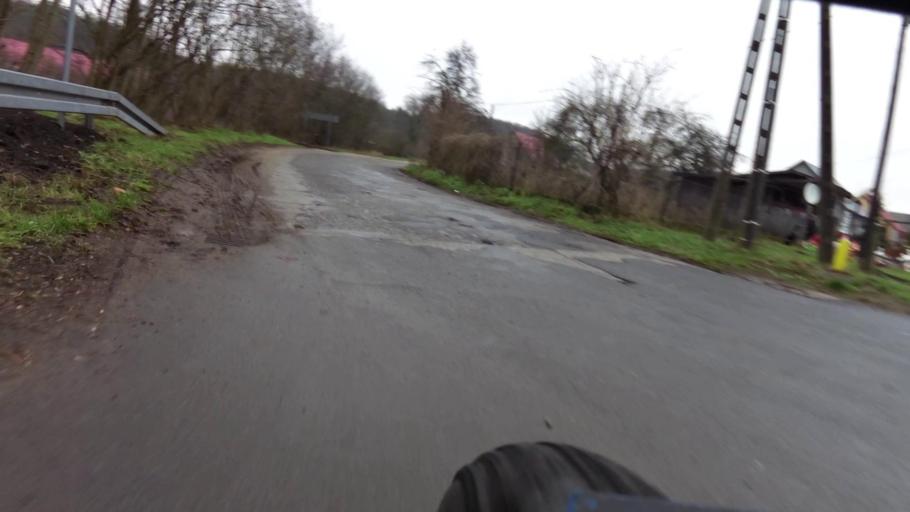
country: PL
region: Lubusz
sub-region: Powiat gorzowski
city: Kostrzyn nad Odra
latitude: 52.6212
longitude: 14.7096
